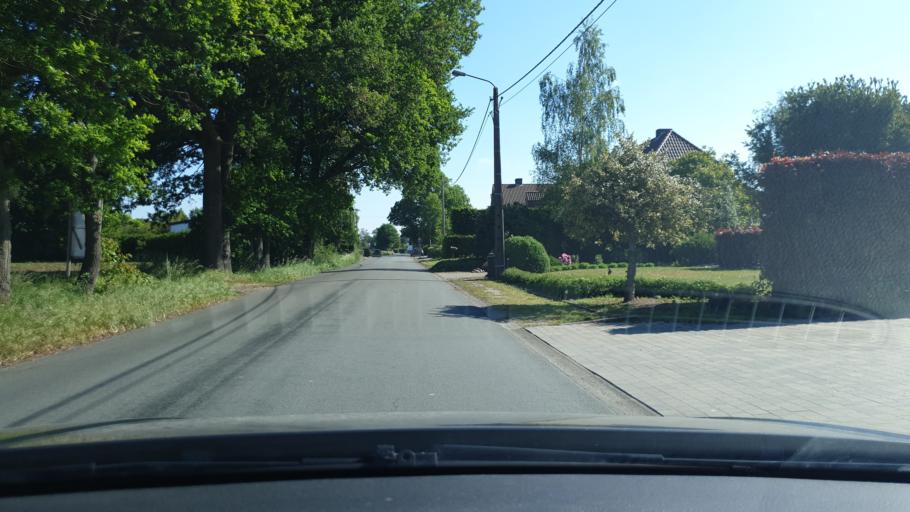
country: BE
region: Flanders
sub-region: Provincie Antwerpen
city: Westerlo
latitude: 51.1488
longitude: 4.9300
